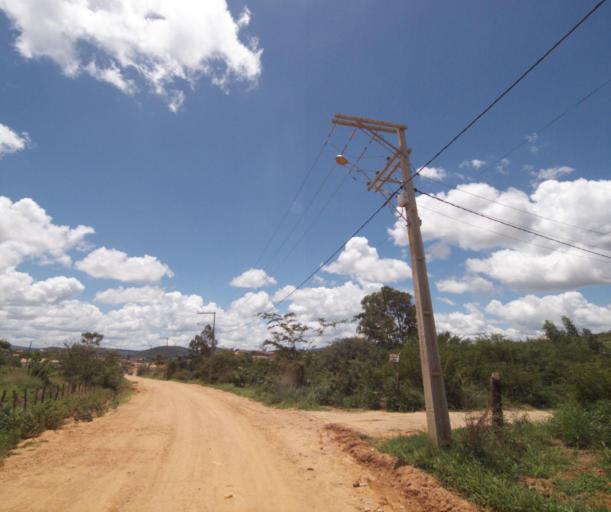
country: BR
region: Bahia
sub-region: Pocoes
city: Pocoes
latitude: -14.3750
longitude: -40.4972
